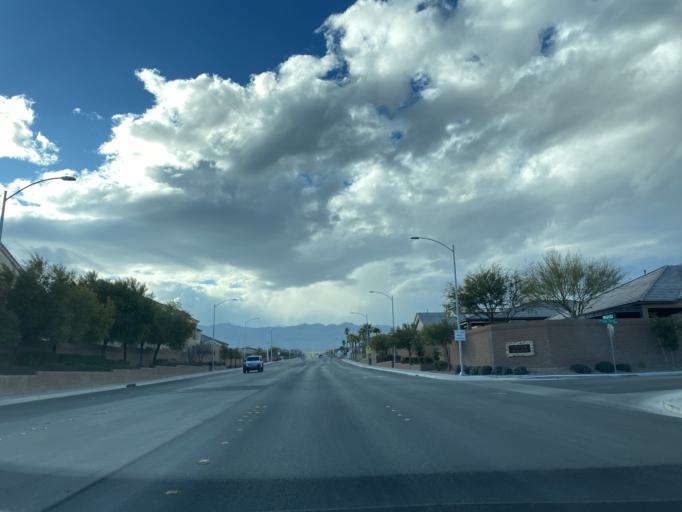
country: US
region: Nevada
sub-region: Clark County
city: Summerlin South
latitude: 36.2846
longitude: -115.3038
